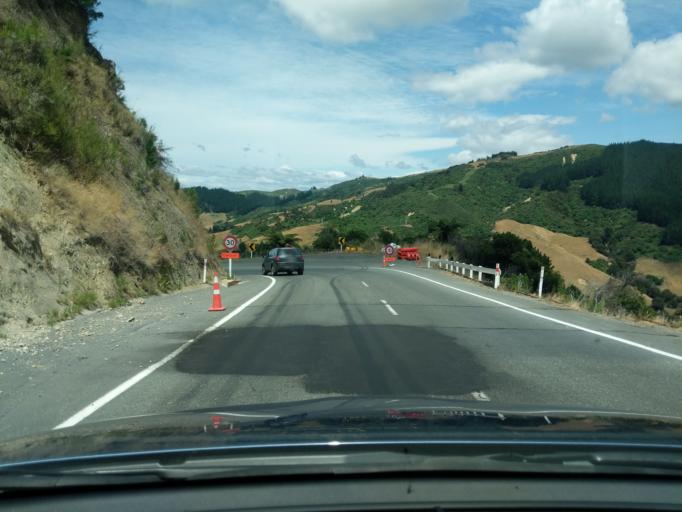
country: NZ
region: Tasman
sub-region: Tasman District
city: Motueka
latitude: -41.0465
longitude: 172.9561
